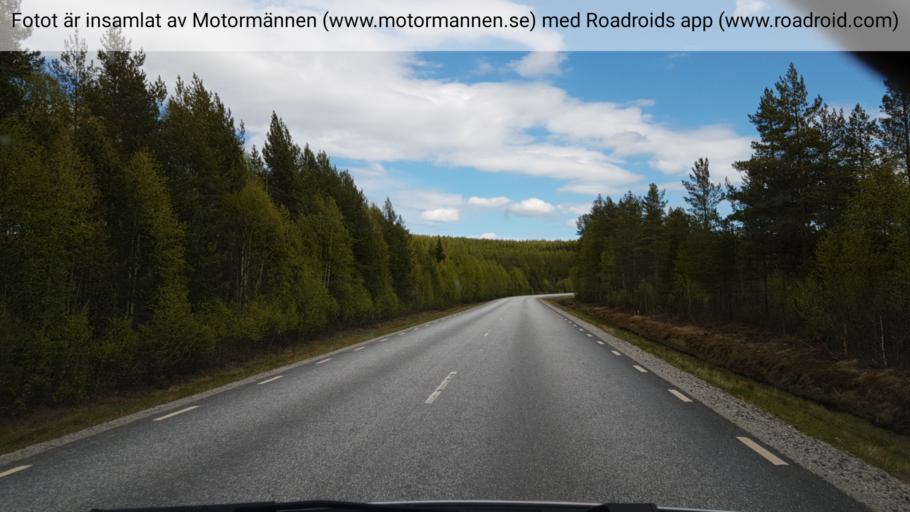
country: SE
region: Vaesterbotten
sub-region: Vindelns Kommun
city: Vindeln
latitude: 64.2075
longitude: 19.4558
